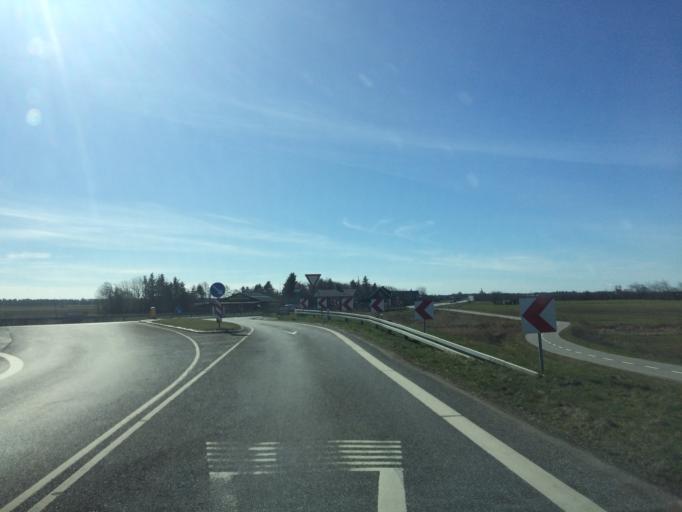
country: DK
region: Central Jutland
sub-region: Holstebro Kommune
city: Ulfborg
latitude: 56.2911
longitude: 8.3382
